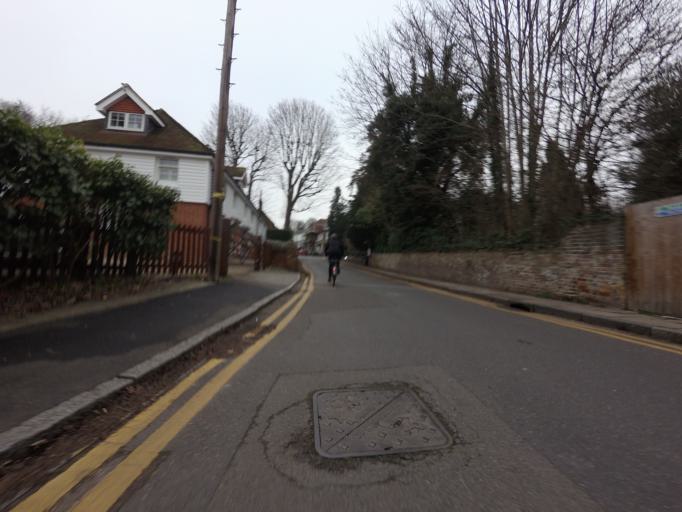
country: GB
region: England
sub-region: Kent
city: Eynsford
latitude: 51.3816
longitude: 0.2199
